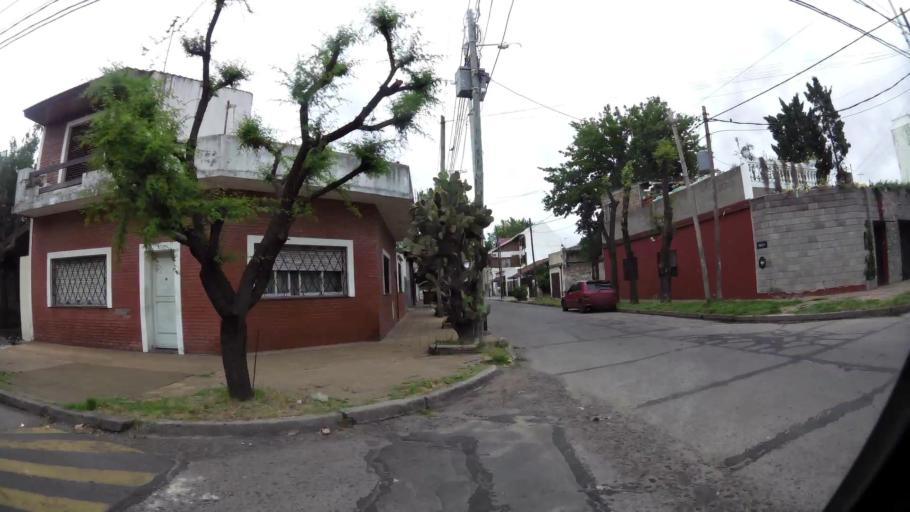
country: AR
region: Buenos Aires
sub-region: Partido de Lanus
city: Lanus
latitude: -34.6847
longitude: -58.3843
